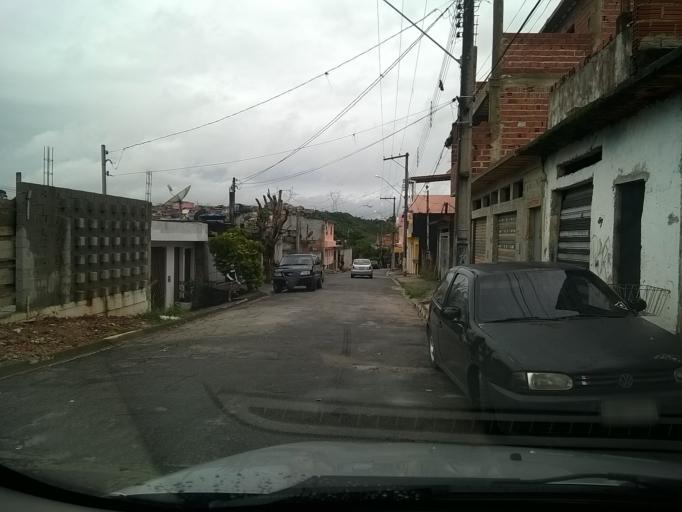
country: BR
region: Sao Paulo
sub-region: Francisco Morato
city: Francisco Morato
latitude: -23.2987
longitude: -46.7391
